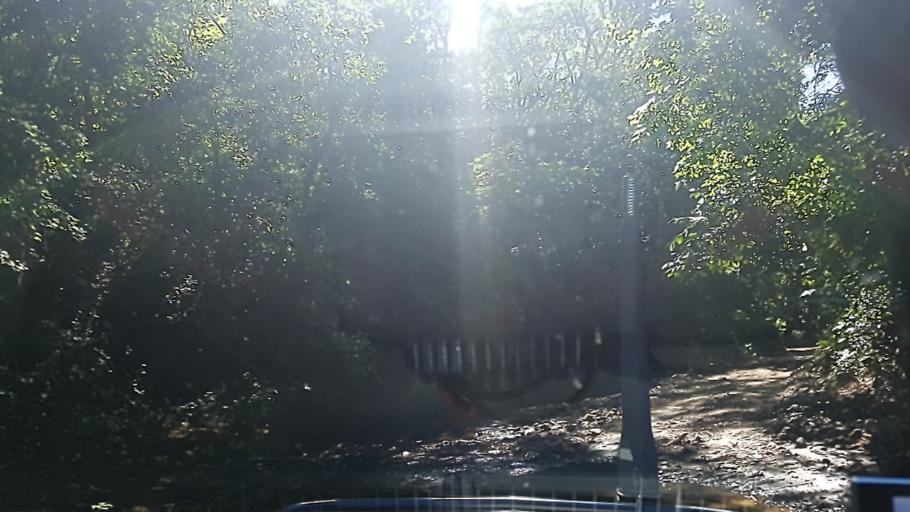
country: NI
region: Rivas
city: Tola
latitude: 11.5573
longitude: -86.0885
